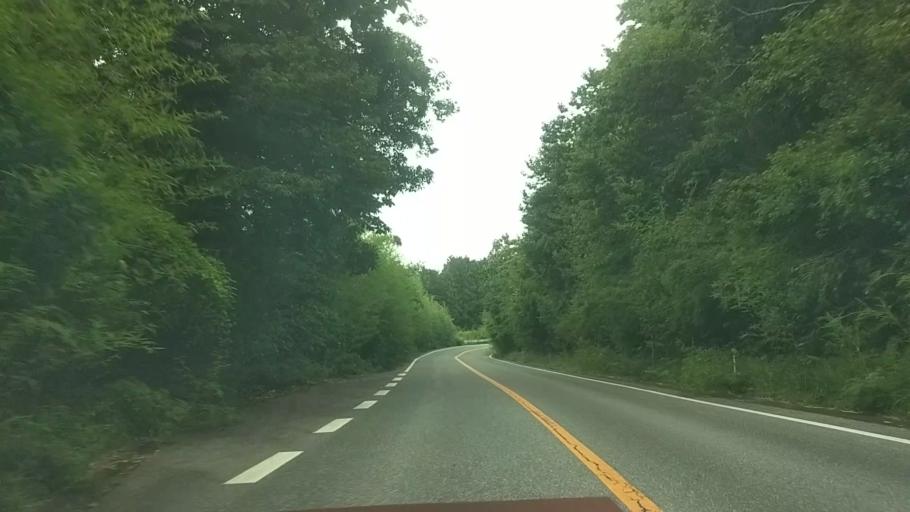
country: JP
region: Chiba
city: Kimitsu
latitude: 35.2387
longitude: 140.0068
